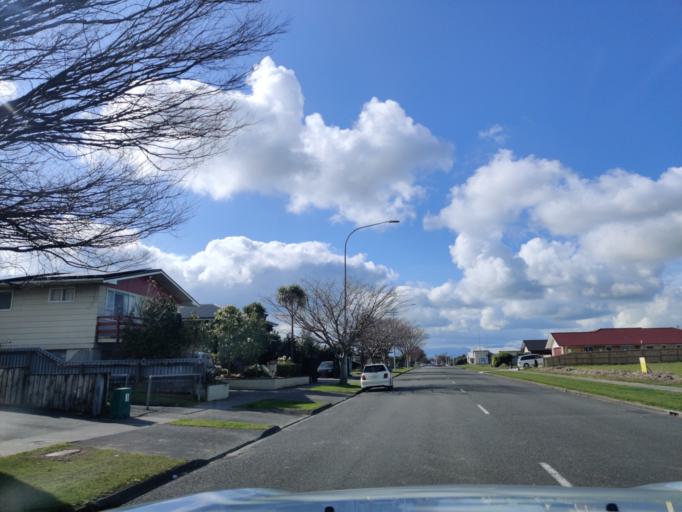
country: NZ
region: Manawatu-Wanganui
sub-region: Palmerston North City
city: Palmerston North
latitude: -40.3370
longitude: 175.6047
